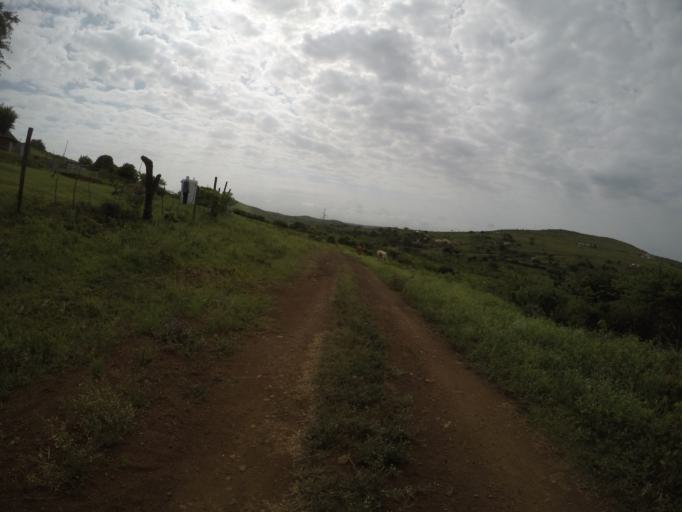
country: ZA
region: KwaZulu-Natal
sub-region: uThungulu District Municipality
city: Empangeni
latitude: -28.6277
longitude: 31.9026
